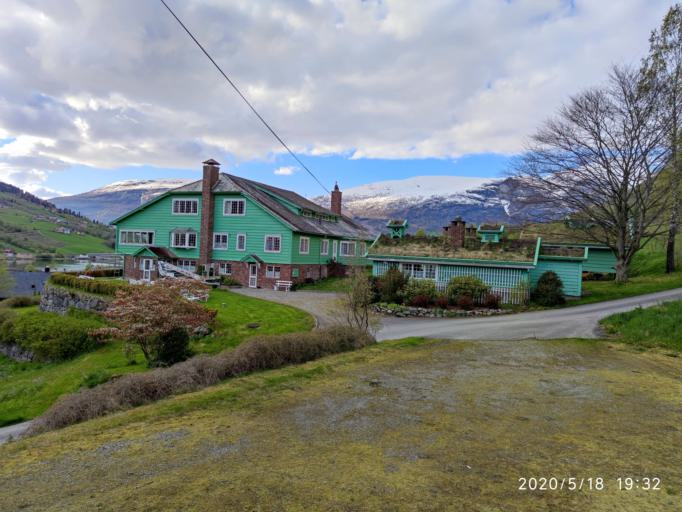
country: NO
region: Sogn og Fjordane
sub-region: Stryn
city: Stryn
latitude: 61.8320
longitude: 6.8134
